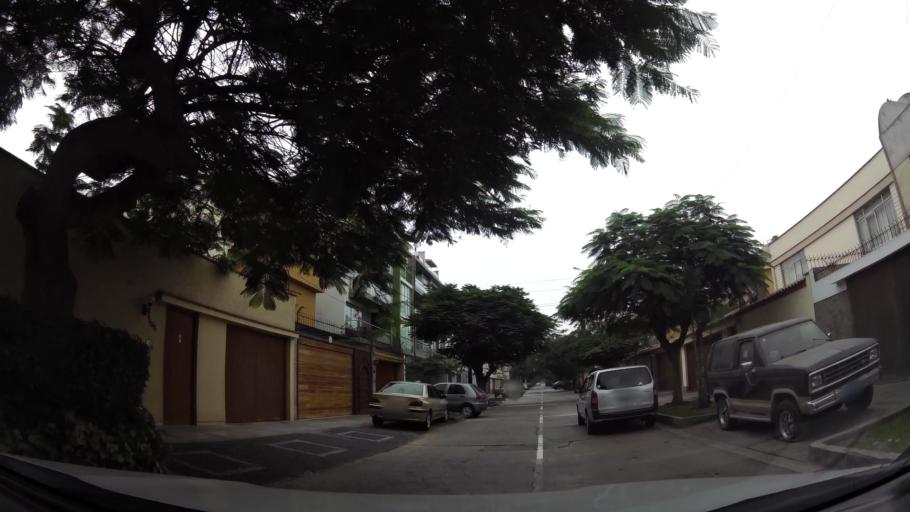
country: PE
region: Lima
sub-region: Lima
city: Surco
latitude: -12.1190
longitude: -76.9925
